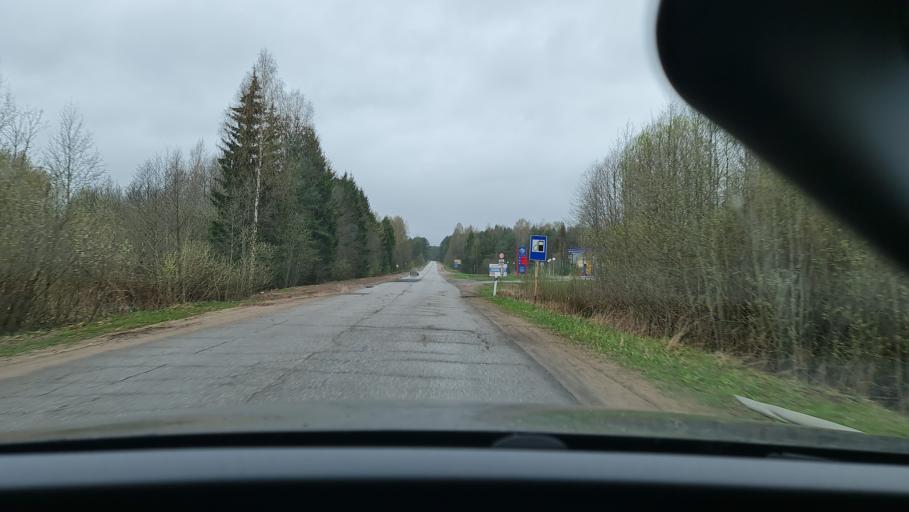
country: RU
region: Novgorod
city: Demyansk
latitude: 57.6588
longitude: 32.5026
